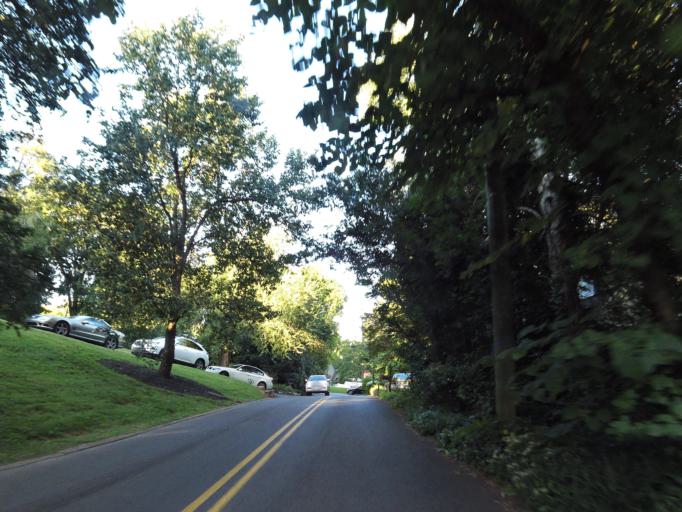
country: US
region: Tennessee
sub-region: Knox County
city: Knoxville
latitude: 35.9387
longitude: -83.9699
